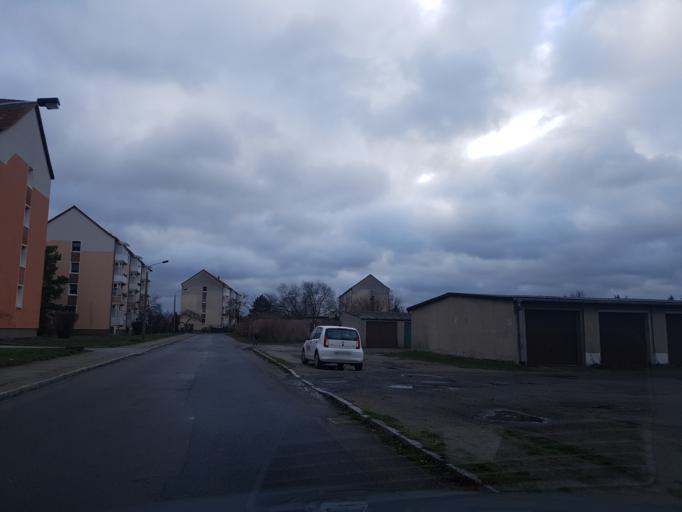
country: DE
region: Brandenburg
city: Herzberg
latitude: 51.6858
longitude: 13.2234
